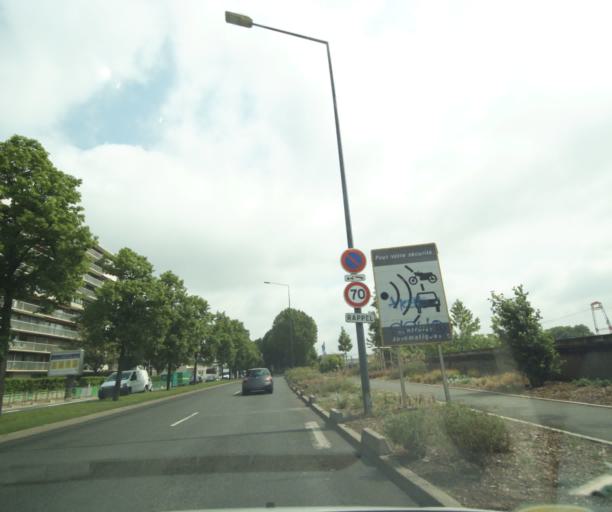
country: FR
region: Ile-de-France
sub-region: Departement des Hauts-de-Seine
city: Levallois-Perret
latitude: 48.9060
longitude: 2.2899
